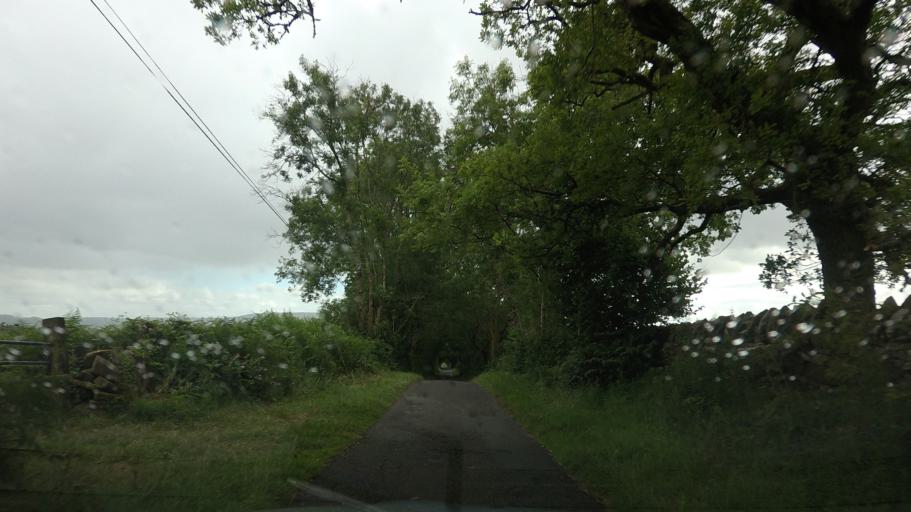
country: GB
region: Scotland
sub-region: Stirling
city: Killearn
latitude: 56.0797
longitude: -4.4498
